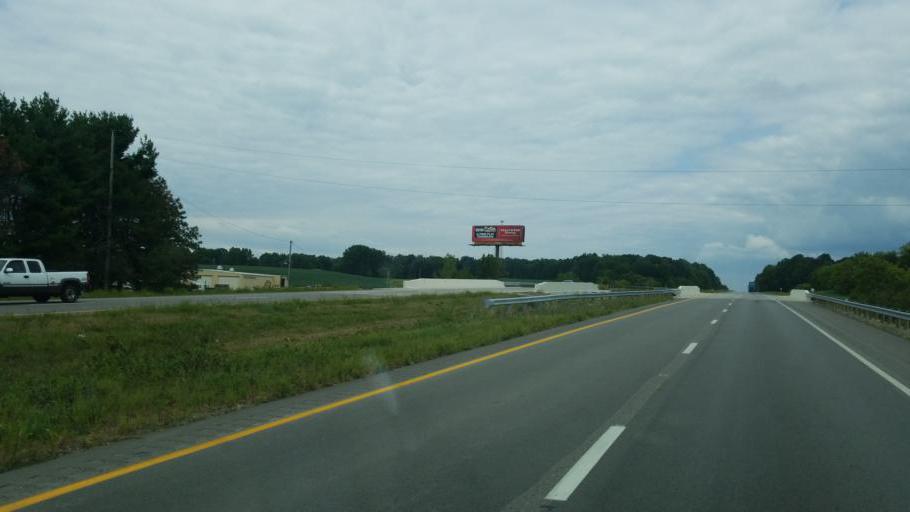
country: US
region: Ohio
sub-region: Columbiana County
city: Leetonia
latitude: 40.8271
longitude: -80.7418
